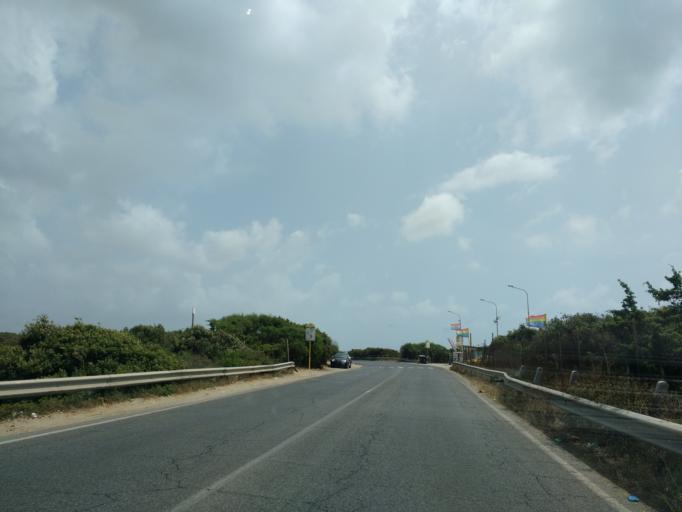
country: IT
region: Latium
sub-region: Citta metropolitana di Roma Capitale
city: Torvaianica
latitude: 41.6657
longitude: 12.4046
